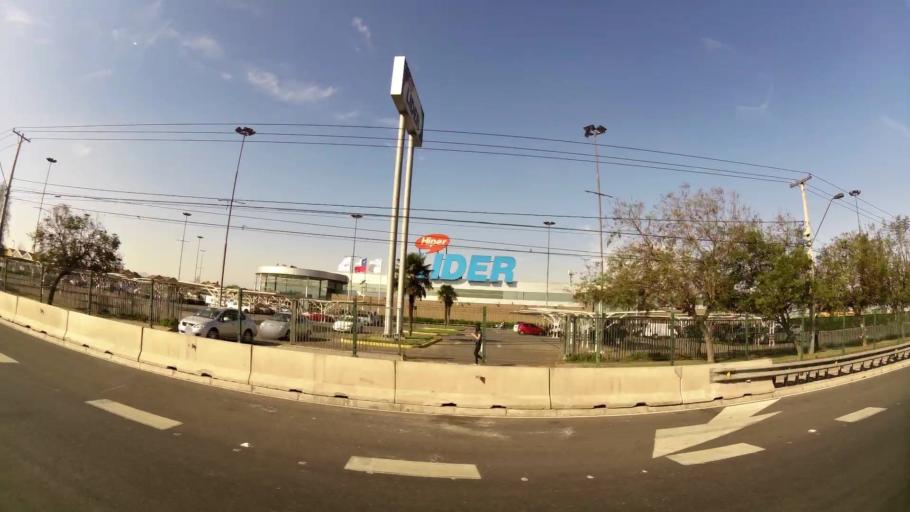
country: CL
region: Santiago Metropolitan
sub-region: Provincia de Santiago
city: Lo Prado
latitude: -33.4722
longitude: -70.7596
